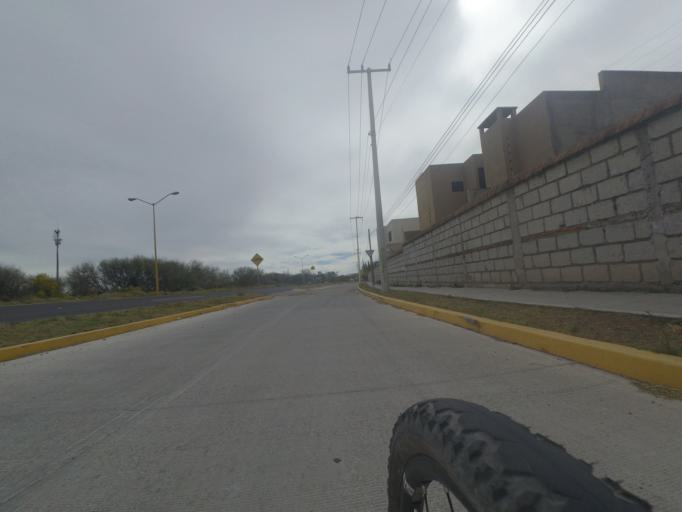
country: MX
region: Aguascalientes
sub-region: Aguascalientes
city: La Loma de los Negritos
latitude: 21.8476
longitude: -102.3529
